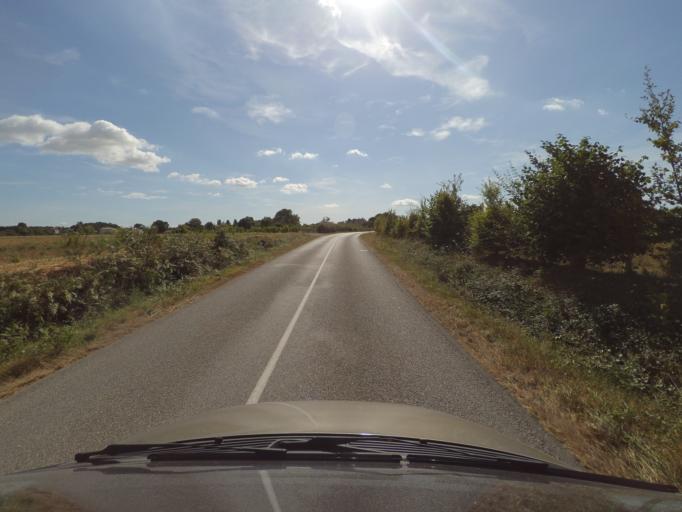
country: FR
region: Pays de la Loire
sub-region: Departement de la Loire-Atlantique
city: Le Bignon
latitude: 47.0917
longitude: -1.5216
